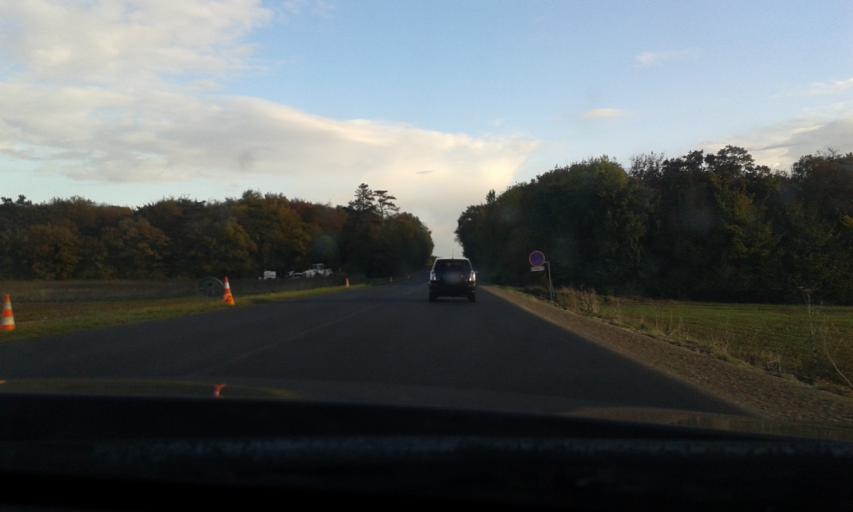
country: FR
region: Centre
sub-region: Departement d'Eure-et-Loir
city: Sours
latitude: 48.3972
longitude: 1.5596
